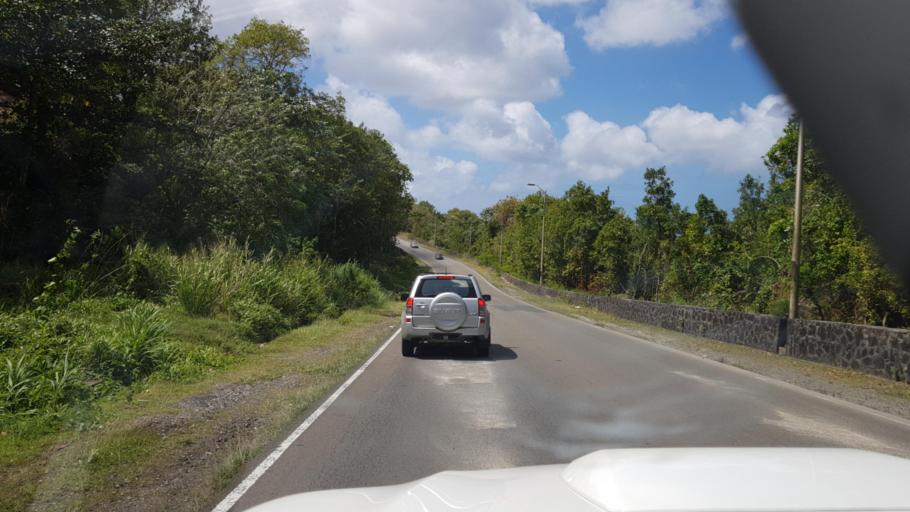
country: LC
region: Castries Quarter
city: Castries
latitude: 14.0048
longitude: -61.0055
